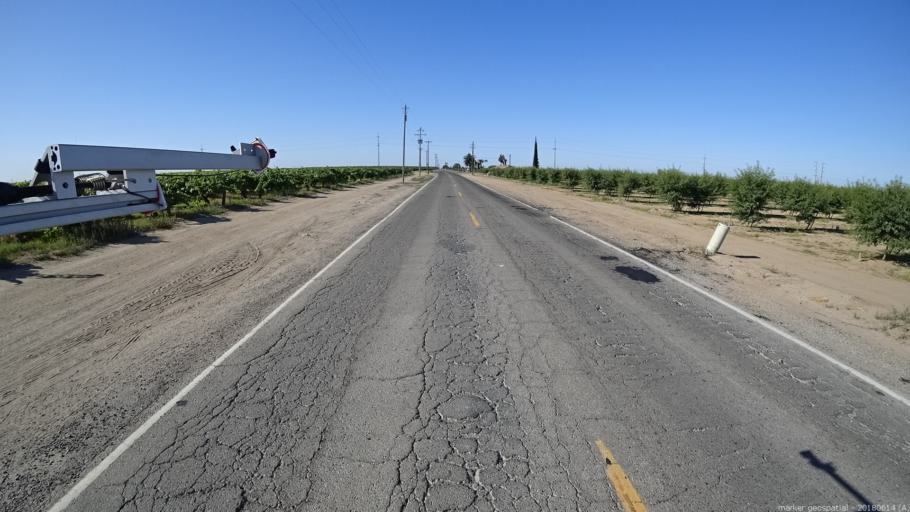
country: US
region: California
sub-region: Madera County
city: Madera
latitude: 36.9250
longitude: -120.1294
